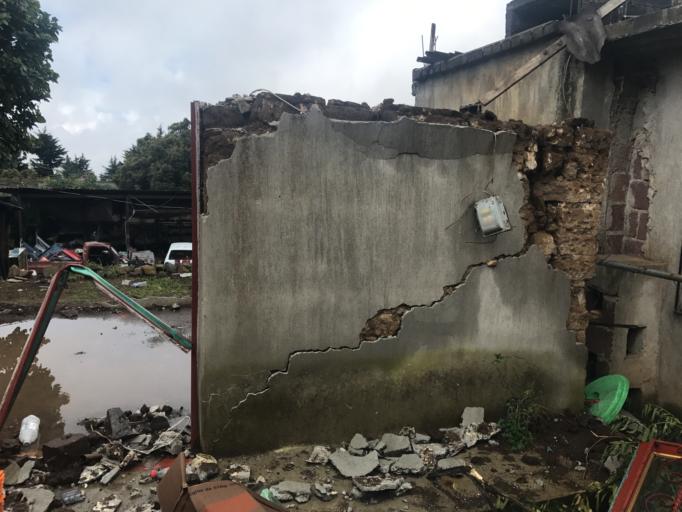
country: MX
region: Morelos
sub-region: Tetela del Volcan
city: Tetela del Volcan
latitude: 18.9059
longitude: -98.7224
